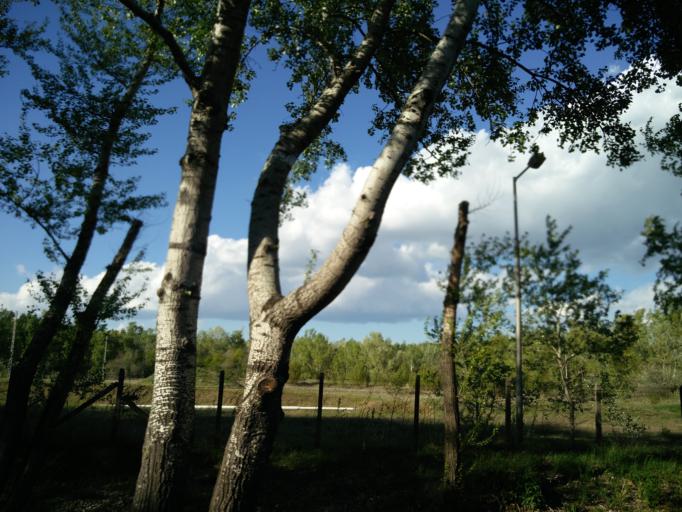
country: HU
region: Pest
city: Vecses
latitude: 47.4211
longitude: 19.2511
